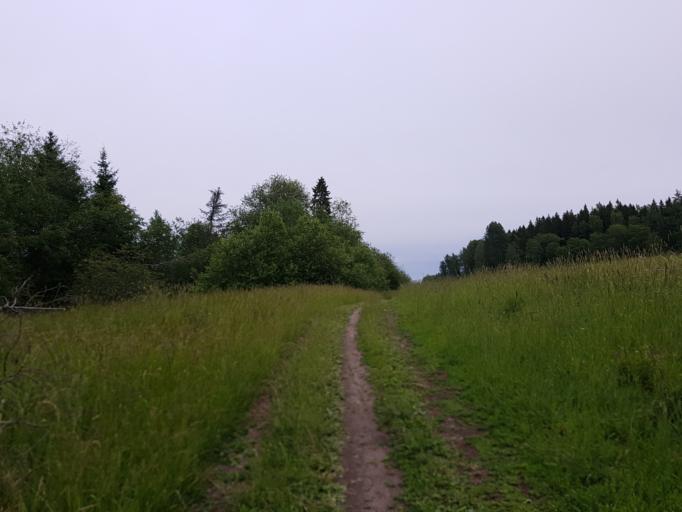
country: FI
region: Uusimaa
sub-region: Helsinki
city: Helsinki
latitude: 60.2703
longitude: 24.9092
